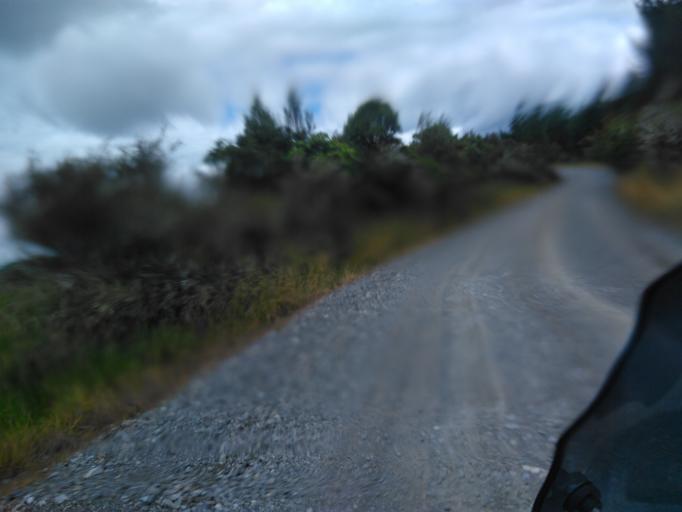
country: NZ
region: Gisborne
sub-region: Gisborne District
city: Gisborne
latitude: -38.1562
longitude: 178.1335
